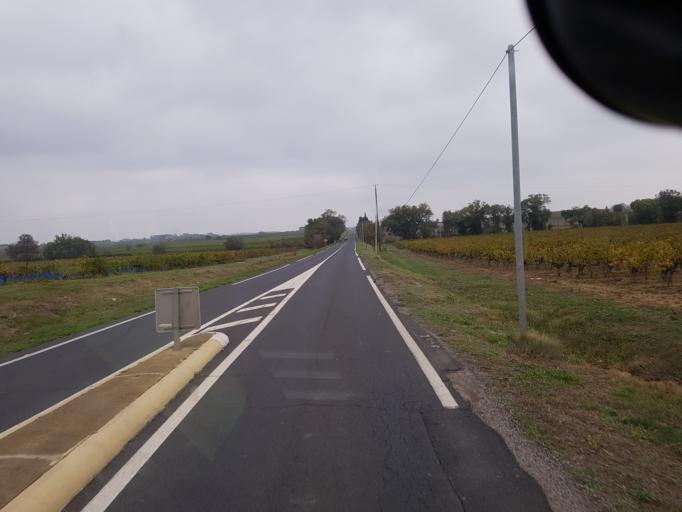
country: FR
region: Languedoc-Roussillon
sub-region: Departement de l'Herault
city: Pinet
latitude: 43.4040
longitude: 3.5401
